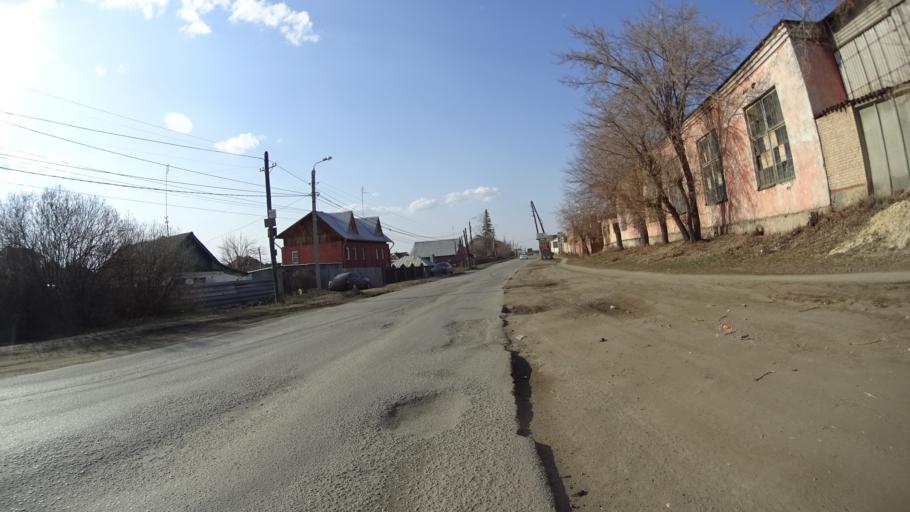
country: RU
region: Chelyabinsk
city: Novosineglazovskiy
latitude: 55.1073
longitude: 61.3357
